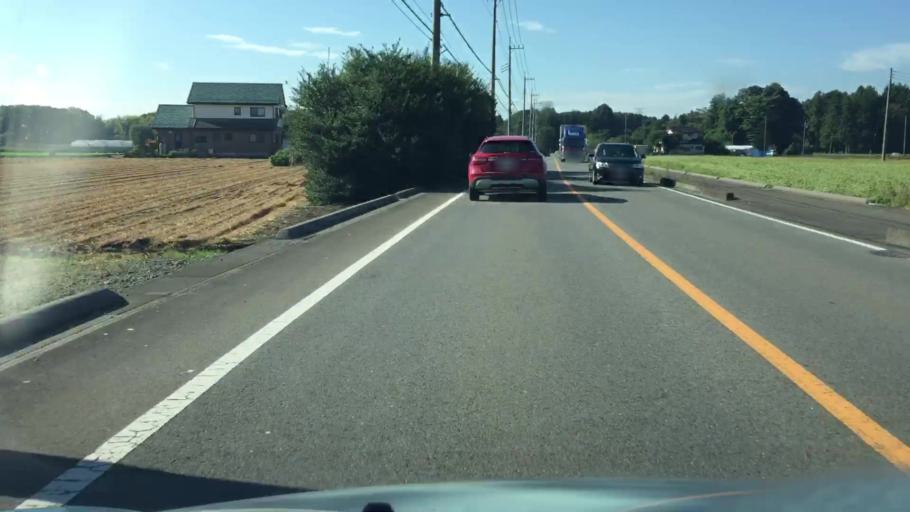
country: JP
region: Tochigi
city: Utsunomiya-shi
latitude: 36.5801
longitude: 139.9812
